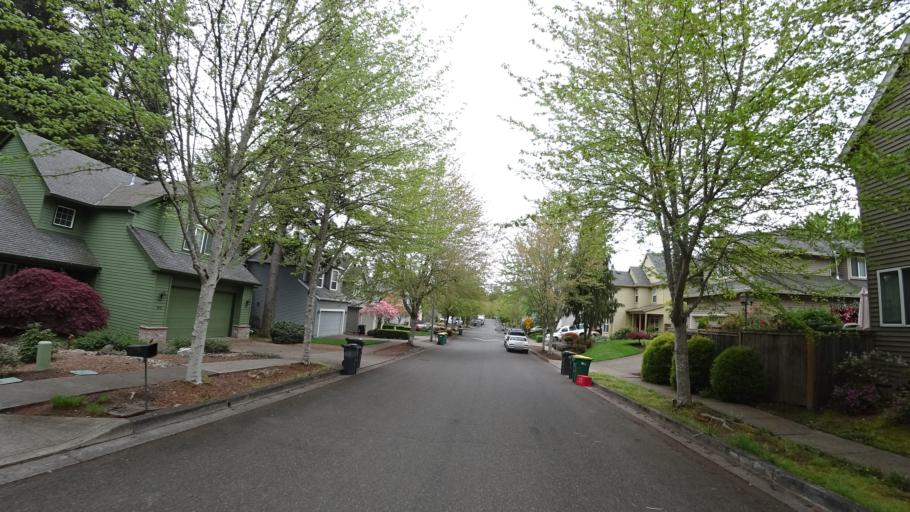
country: US
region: Oregon
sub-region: Washington County
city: Beaverton
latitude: 45.4499
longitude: -122.8312
